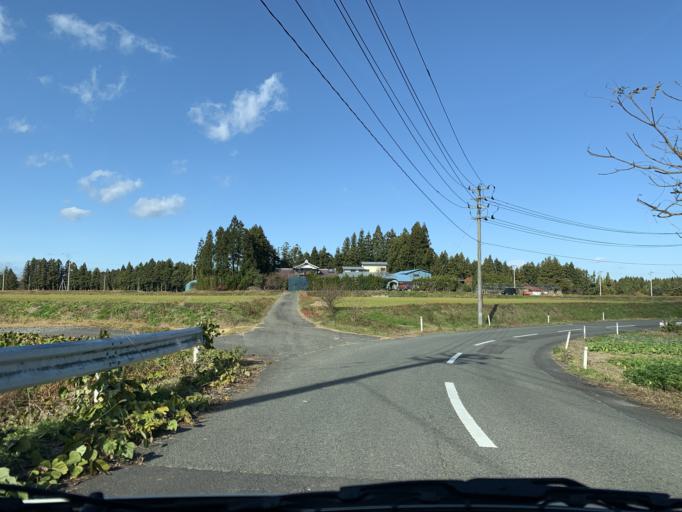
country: JP
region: Iwate
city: Mizusawa
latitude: 39.0681
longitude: 141.1116
